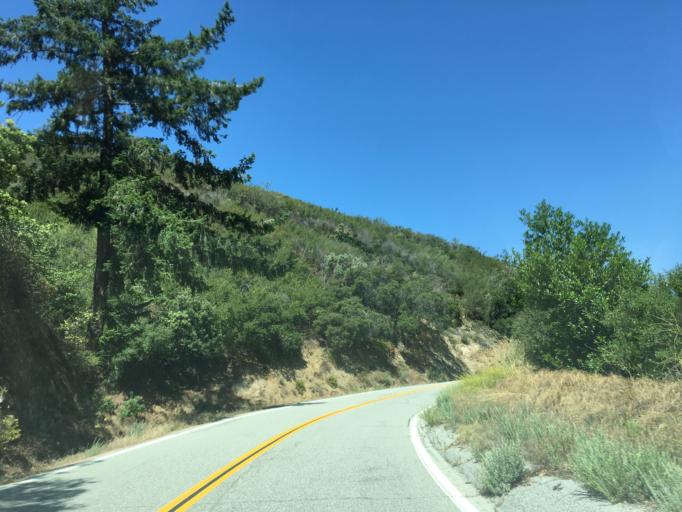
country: US
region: California
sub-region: Los Angeles County
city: Glendora
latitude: 34.2123
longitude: -117.8001
